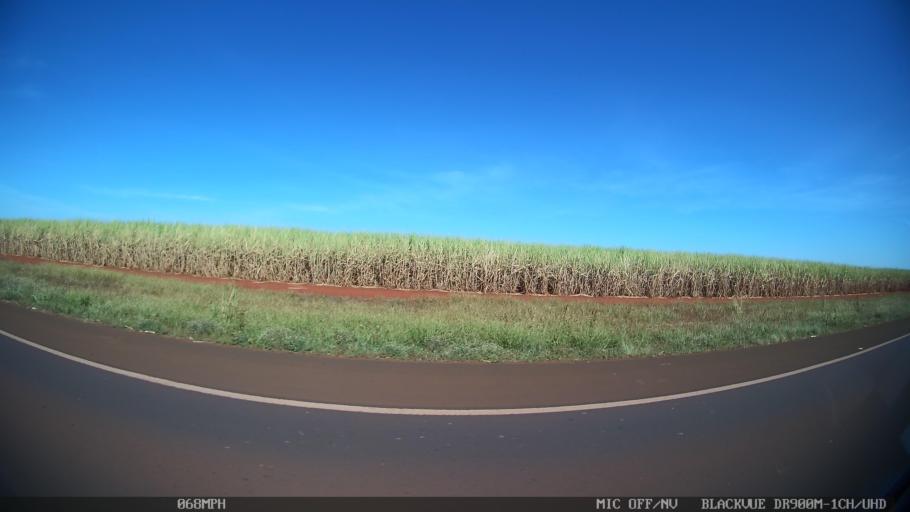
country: BR
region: Sao Paulo
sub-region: Guaira
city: Guaira
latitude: -20.4444
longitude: -48.2758
